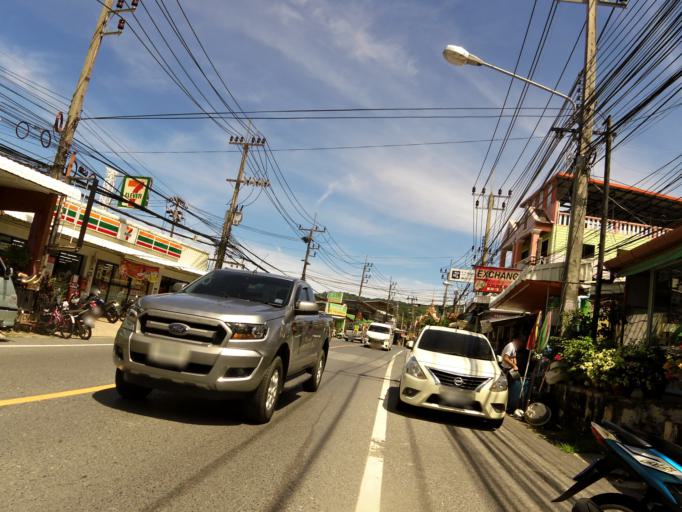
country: TH
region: Phuket
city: Ban Karon
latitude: 7.8462
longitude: 98.2988
